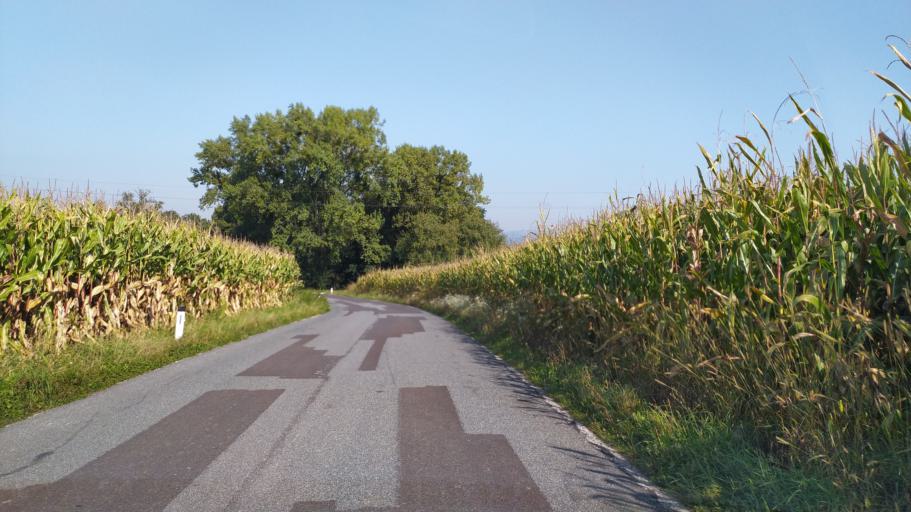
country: AT
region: Lower Austria
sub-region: Politischer Bezirk Amstetten
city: Zeillern
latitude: 48.1514
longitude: 14.7473
